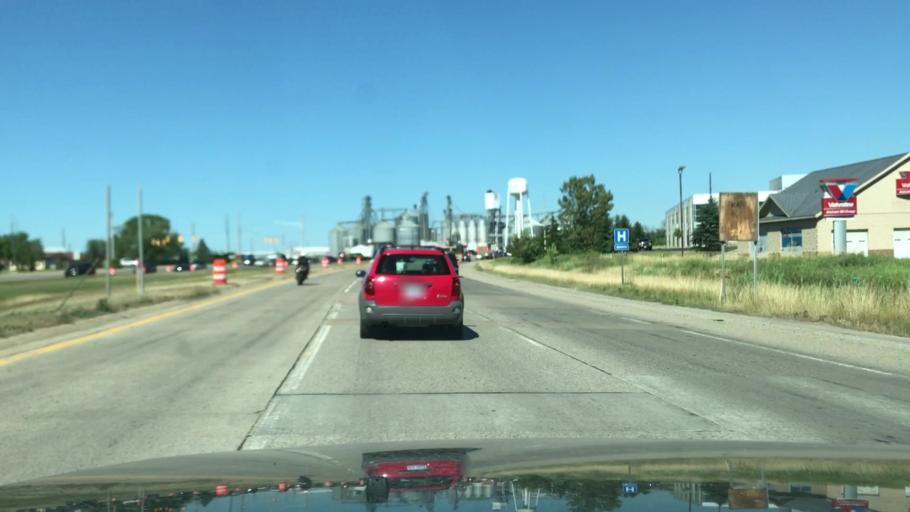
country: US
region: Michigan
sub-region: Ottawa County
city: Zeeland
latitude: 42.8105
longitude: -85.9939
